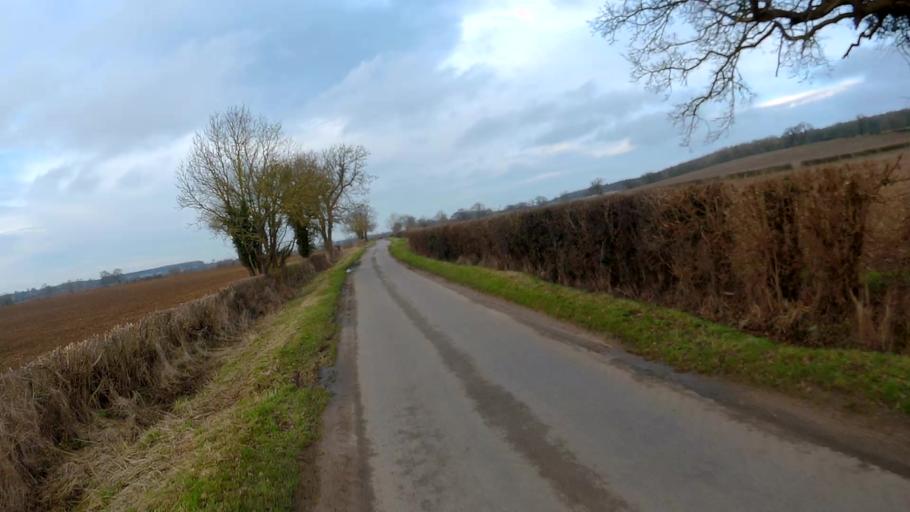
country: GB
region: England
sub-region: Lincolnshire
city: Bourne
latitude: 52.7894
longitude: -0.4263
